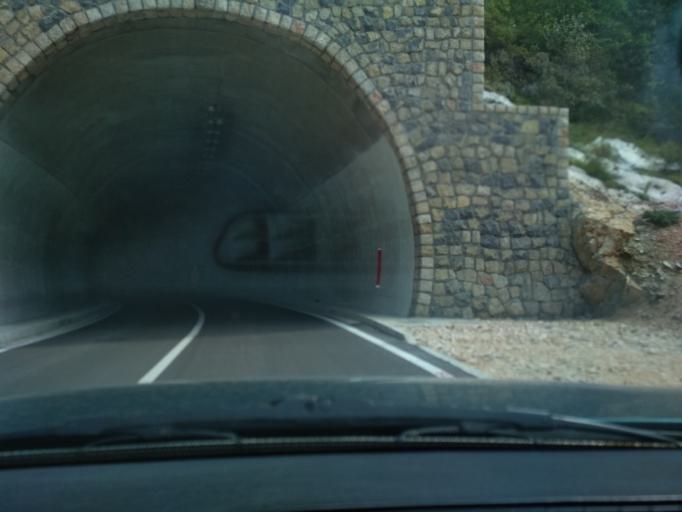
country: ME
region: Cetinje
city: Cetinje
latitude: 42.4350
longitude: 18.8485
